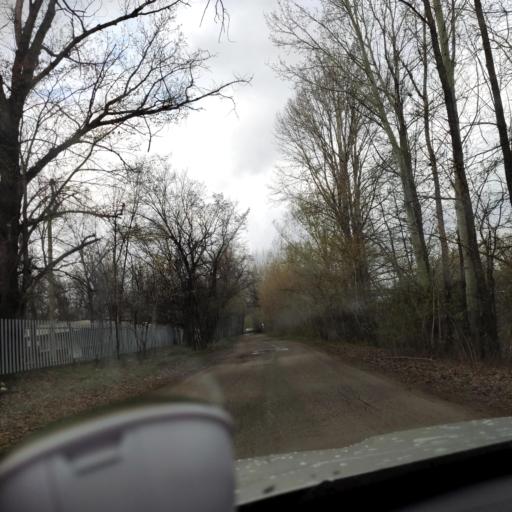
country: RU
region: Samara
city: Novokuybyshevsk
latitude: 53.1395
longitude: 49.9721
